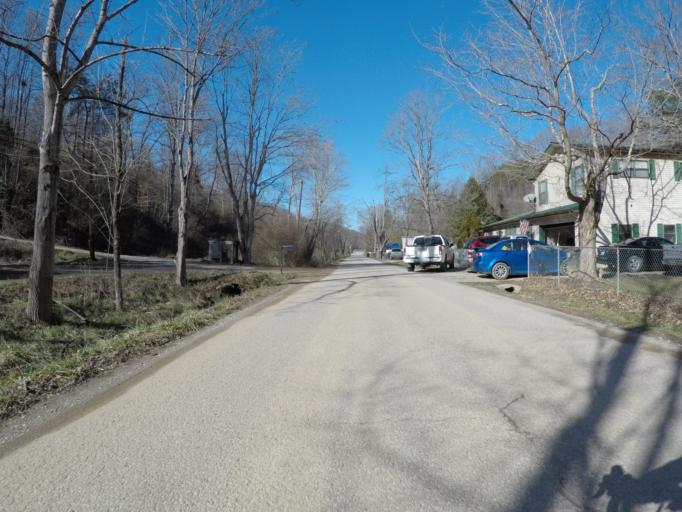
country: US
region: Kentucky
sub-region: Boyd County
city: Catlettsburg
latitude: 38.4083
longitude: -82.6380
